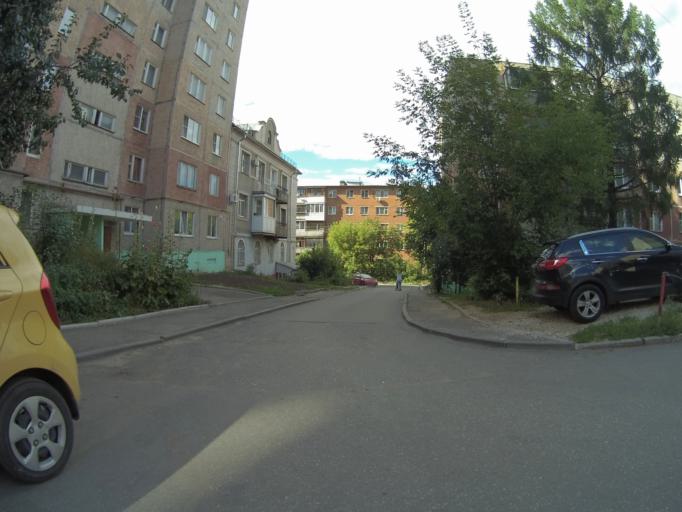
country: RU
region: Vladimir
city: Vladimir
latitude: 56.1194
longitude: 40.3533
